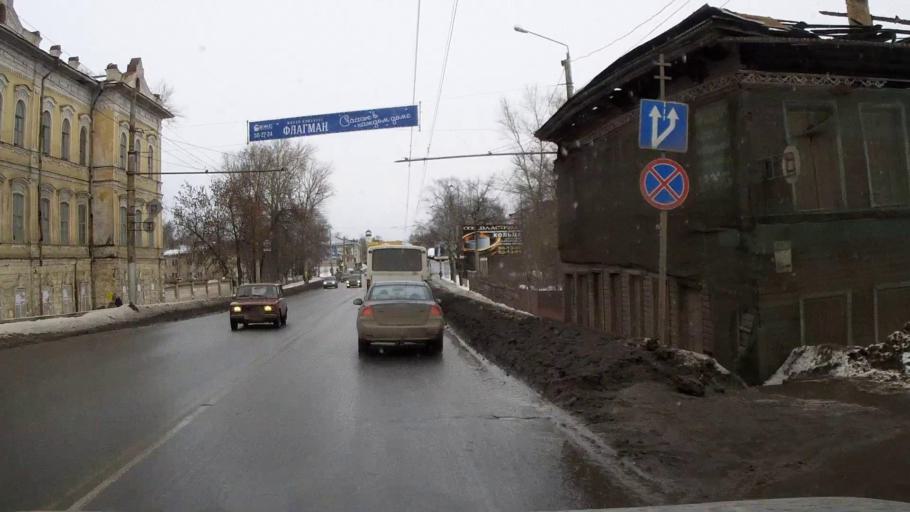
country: RU
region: Vologda
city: Vologda
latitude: 59.2245
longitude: 39.8919
